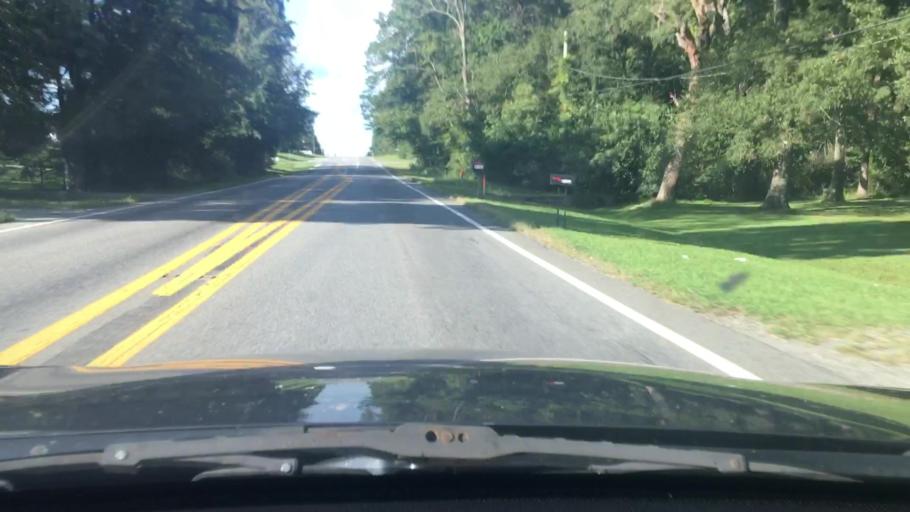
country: US
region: North Carolina
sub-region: Alamance County
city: Green Level
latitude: 36.1665
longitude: -79.3328
